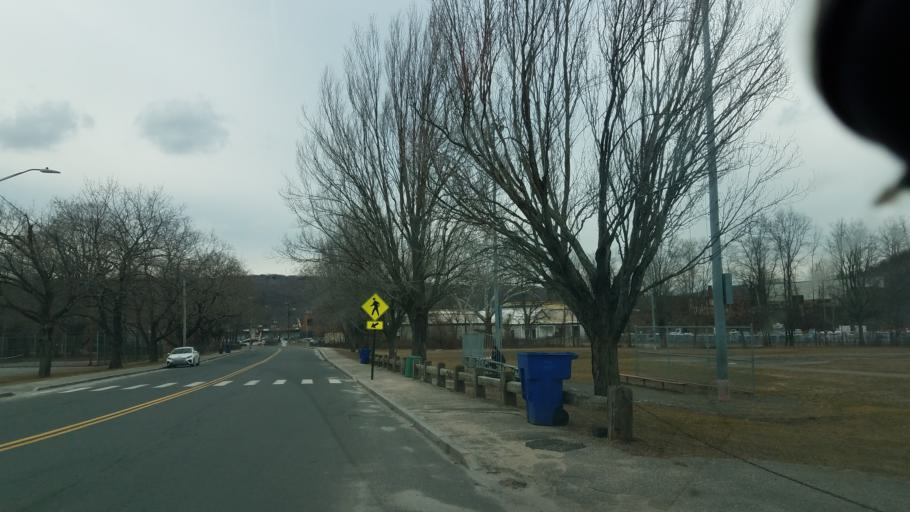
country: US
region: Connecticut
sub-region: New Haven County
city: Waterbury
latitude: 41.5888
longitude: -73.0484
